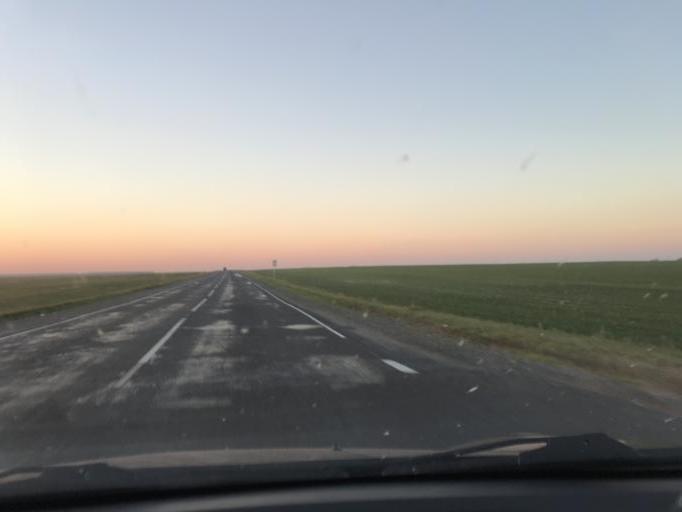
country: BY
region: Gomel
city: Horad Rechytsa
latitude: 52.1717
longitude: 30.5732
